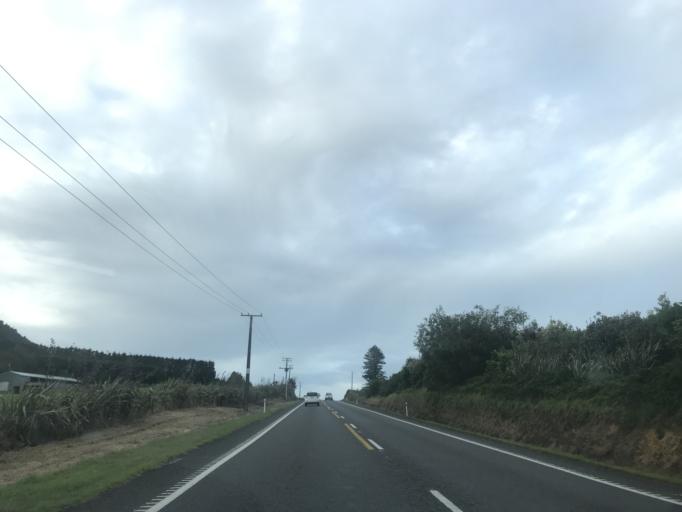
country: NZ
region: Bay of Plenty
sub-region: Western Bay of Plenty District
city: Waihi Beach
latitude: -37.4717
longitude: 175.9353
